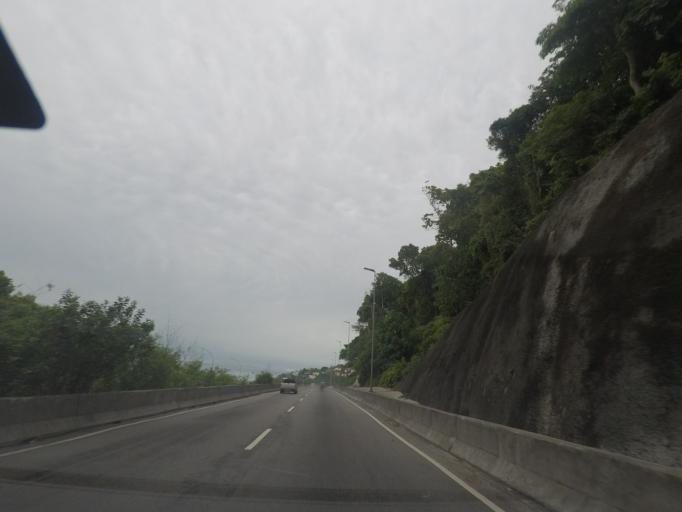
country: BR
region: Rio de Janeiro
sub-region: Rio De Janeiro
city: Rio de Janeiro
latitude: -23.0039
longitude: -43.2779
